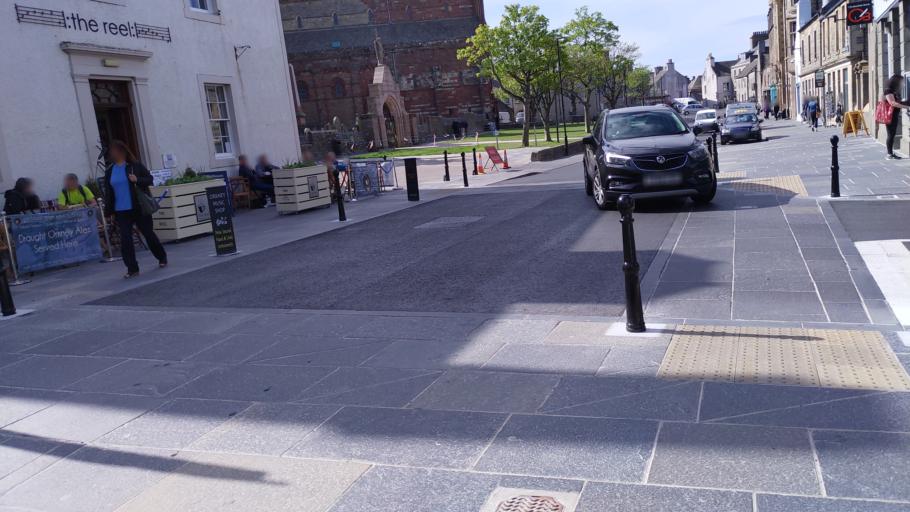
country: GB
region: Scotland
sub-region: Orkney Islands
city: Orkney
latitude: 58.9823
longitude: -2.9598
